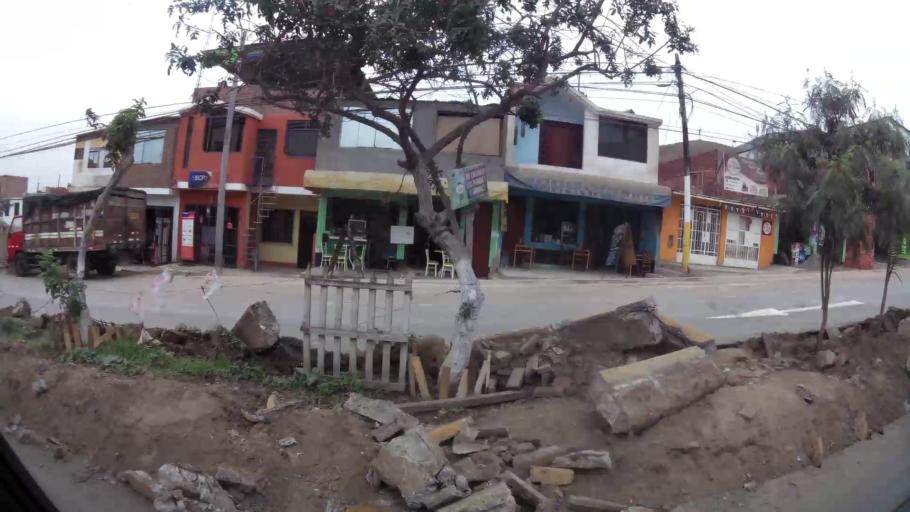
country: PE
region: Lima
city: Ventanilla
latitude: -11.9200
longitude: -77.0877
